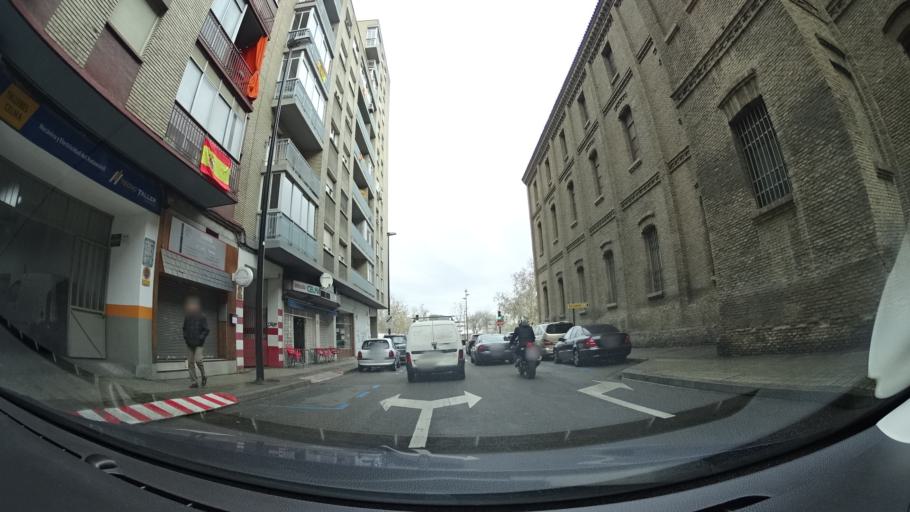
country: ES
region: Aragon
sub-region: Provincia de Zaragoza
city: Zaragoza
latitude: 41.6583
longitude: -0.8891
